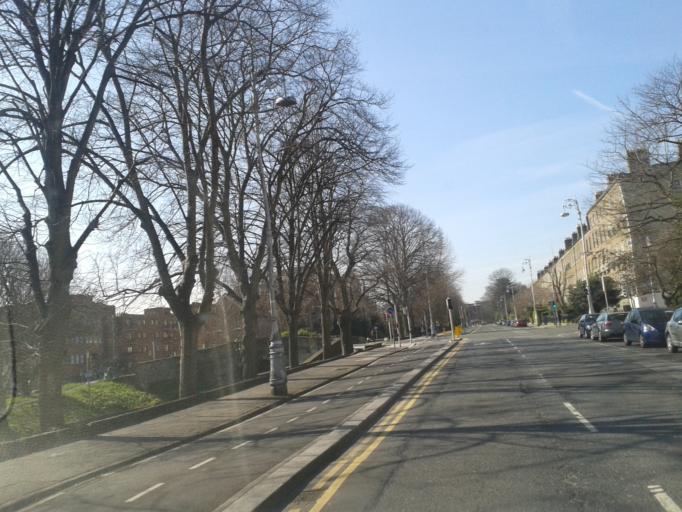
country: IE
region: Leinster
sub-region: Dublin City
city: Dublin
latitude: 53.3369
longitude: -6.2418
